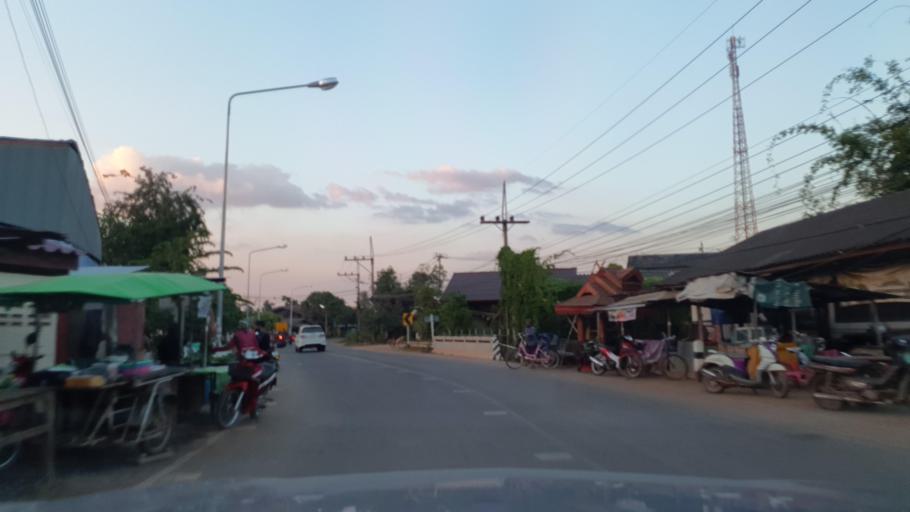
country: TH
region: Phayao
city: Dok Kham Tai
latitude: 19.0348
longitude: 100.0653
